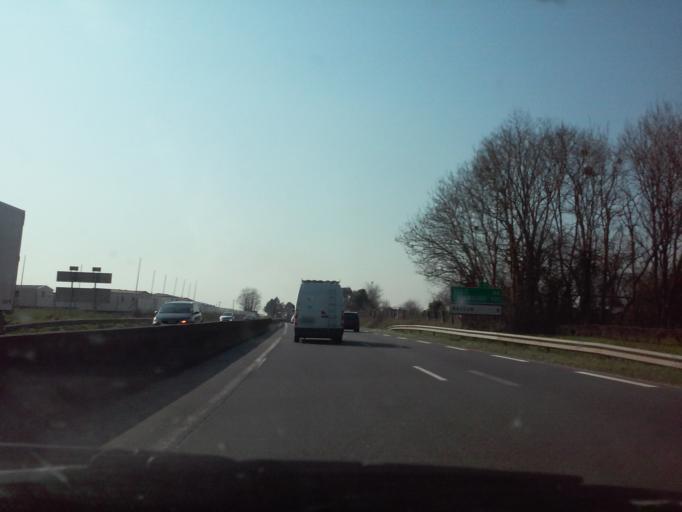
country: FR
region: Lower Normandy
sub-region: Departement du Calvados
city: Tilly-sur-Seulles
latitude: 49.2393
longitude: -0.5967
